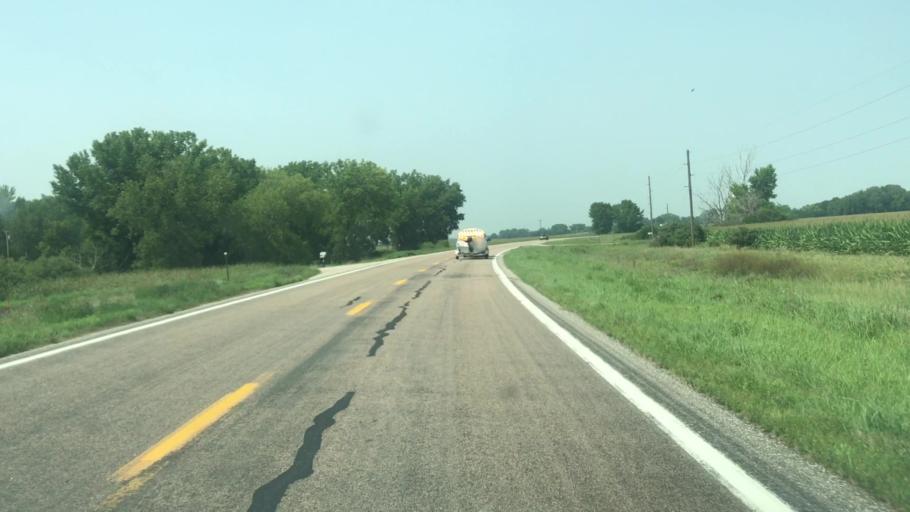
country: US
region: Nebraska
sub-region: Sherman County
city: Loup City
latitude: 41.2345
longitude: -98.9377
